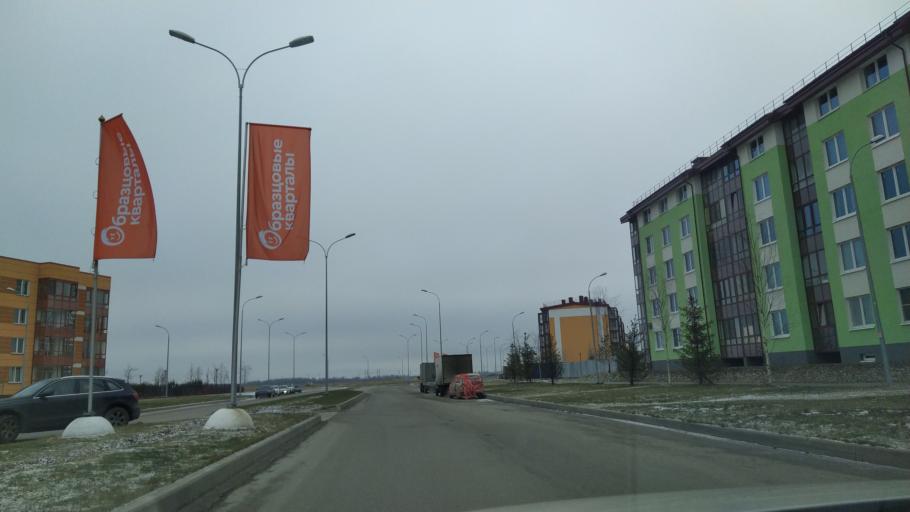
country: RU
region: St.-Petersburg
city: Aleksandrovskaya
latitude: 59.7559
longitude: 30.3664
